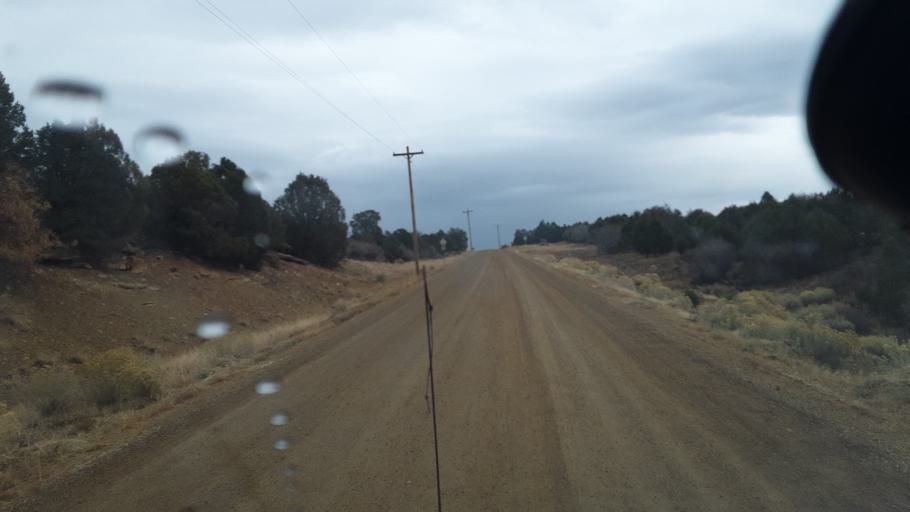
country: US
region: Colorado
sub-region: Montezuma County
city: Mancos
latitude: 37.1983
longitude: -108.1361
